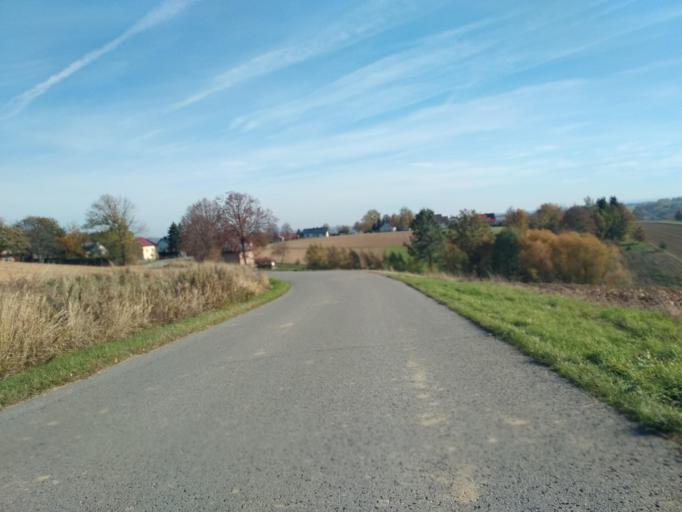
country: PL
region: Subcarpathian Voivodeship
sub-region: Powiat ropczycko-sedziszowski
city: Iwierzyce
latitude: 49.9993
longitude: 21.7313
